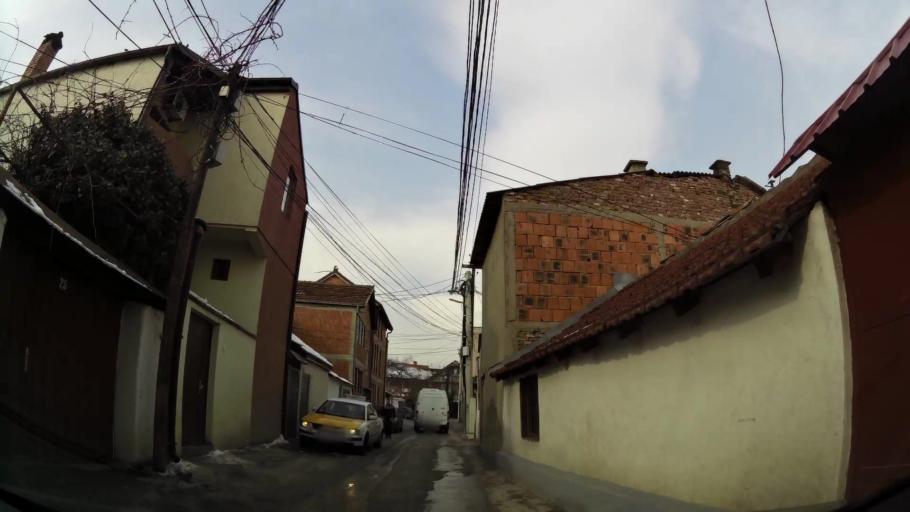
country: MK
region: Cair
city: Cair
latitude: 42.0106
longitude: 21.4365
